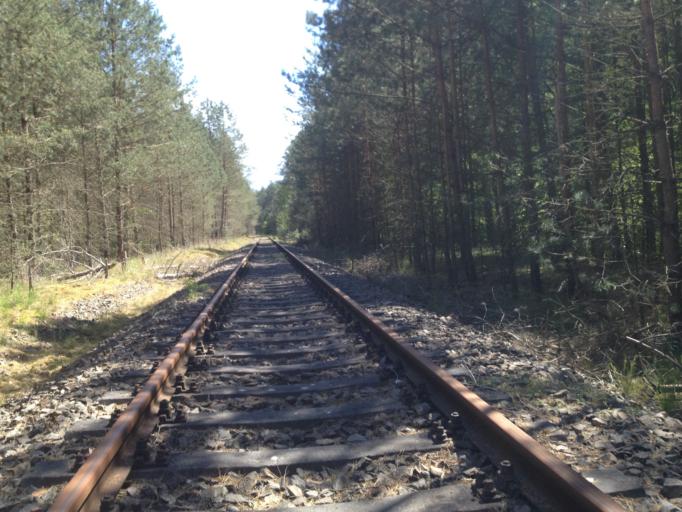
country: DE
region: Brandenburg
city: Lychen
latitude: 53.1761
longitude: 13.3514
